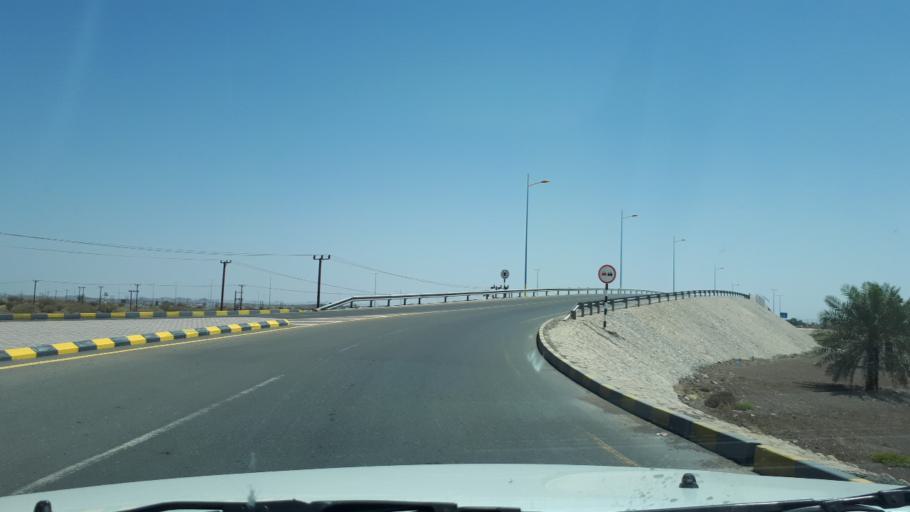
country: OM
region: Muhafazat ad Dakhiliyah
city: Bahla'
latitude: 22.9287
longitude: 57.2565
